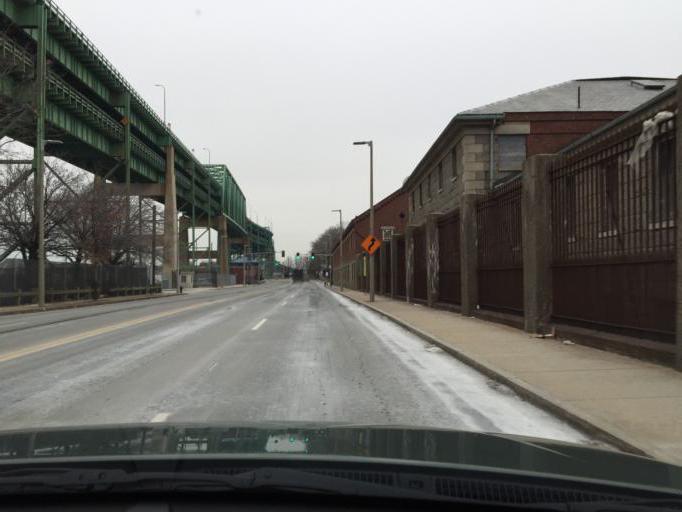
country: US
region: Massachusetts
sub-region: Suffolk County
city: Boston
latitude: 42.3778
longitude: -71.0535
